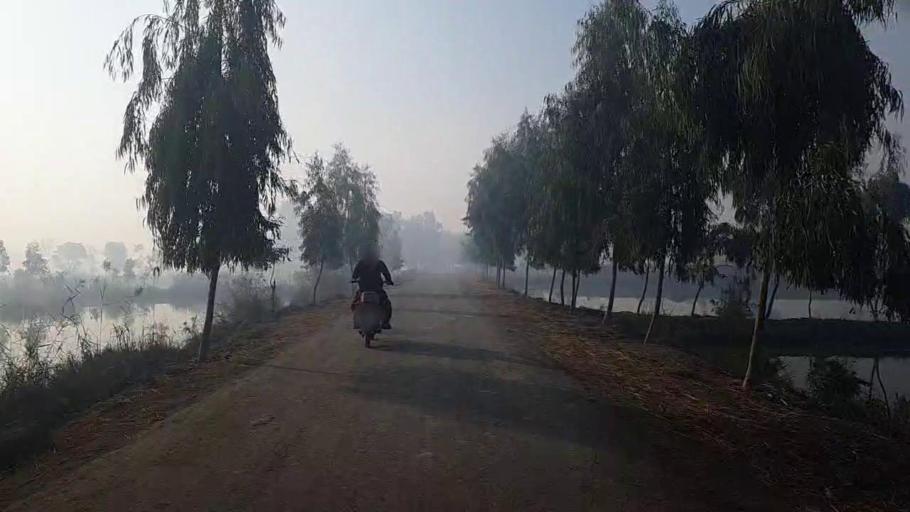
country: PK
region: Sindh
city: Mehar
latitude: 27.1520
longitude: 67.8238
